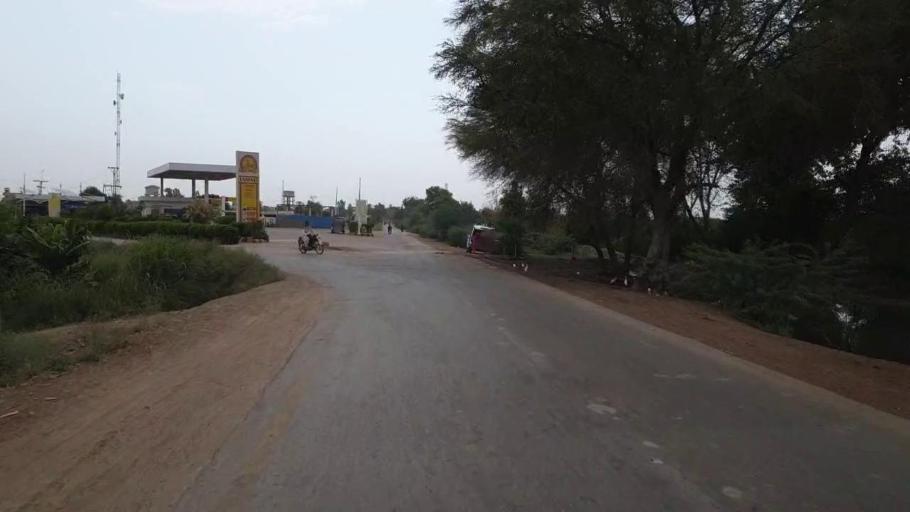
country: PK
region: Sindh
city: Bandhi
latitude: 26.5892
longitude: 68.2930
